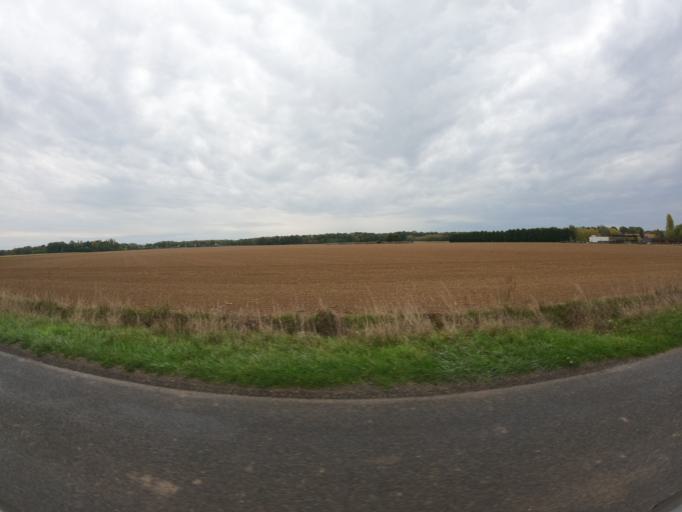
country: FR
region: Ile-de-France
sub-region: Departement de Seine-et-Marne
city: Serris
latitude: 48.8168
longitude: 2.7889
